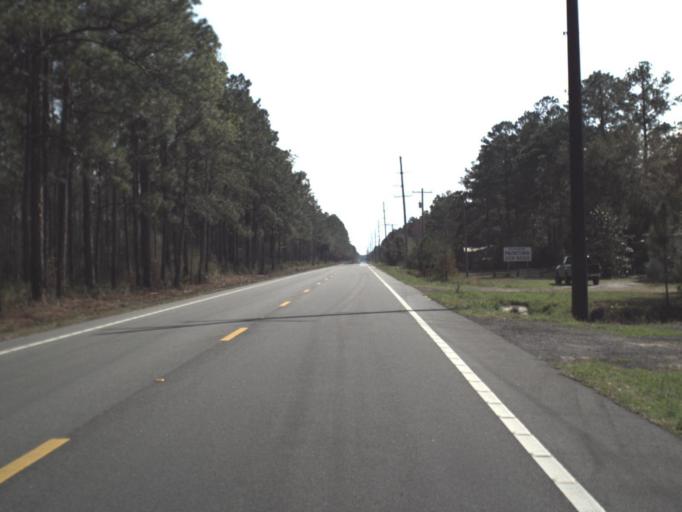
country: US
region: Florida
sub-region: Wakulla County
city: Crawfordville
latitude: 30.0429
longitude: -84.4952
